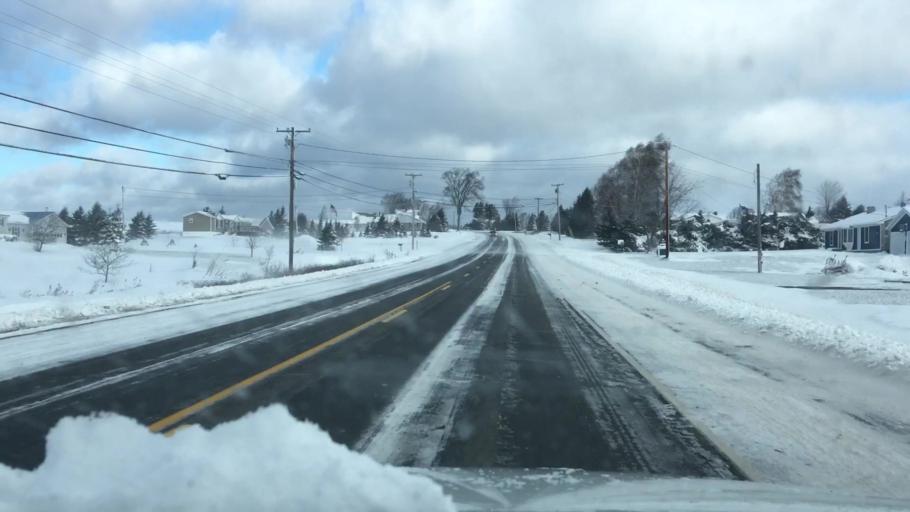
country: US
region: Maine
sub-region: Aroostook County
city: Caribou
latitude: 46.8989
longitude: -68.0154
